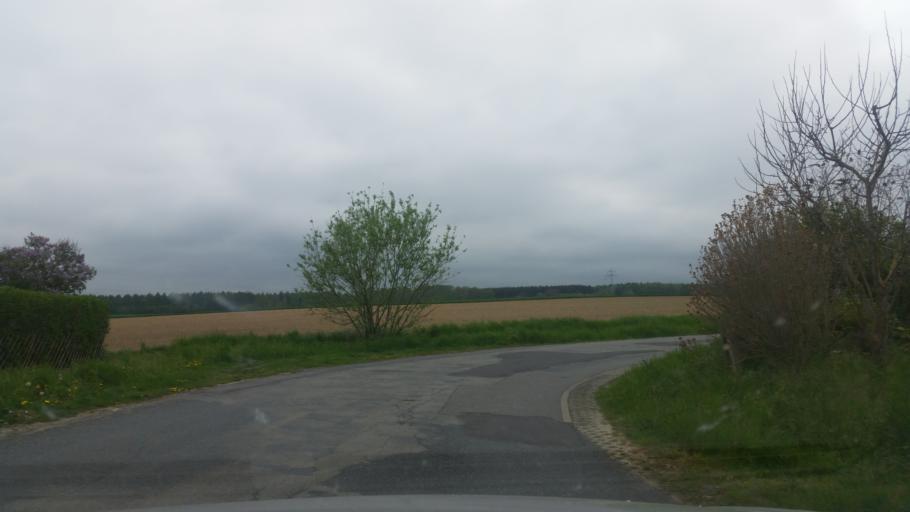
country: DE
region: Lower Saxony
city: Rabke
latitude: 52.2179
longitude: 10.8534
